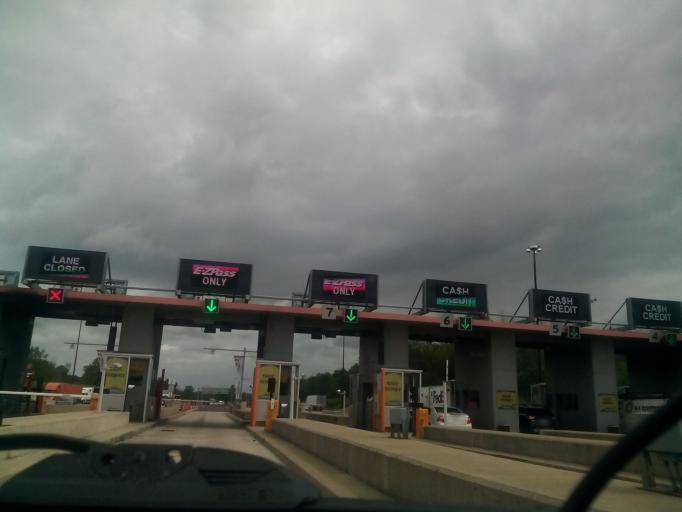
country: US
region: Indiana
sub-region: Steuben County
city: Fremont
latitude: 41.6662
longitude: -84.8536
